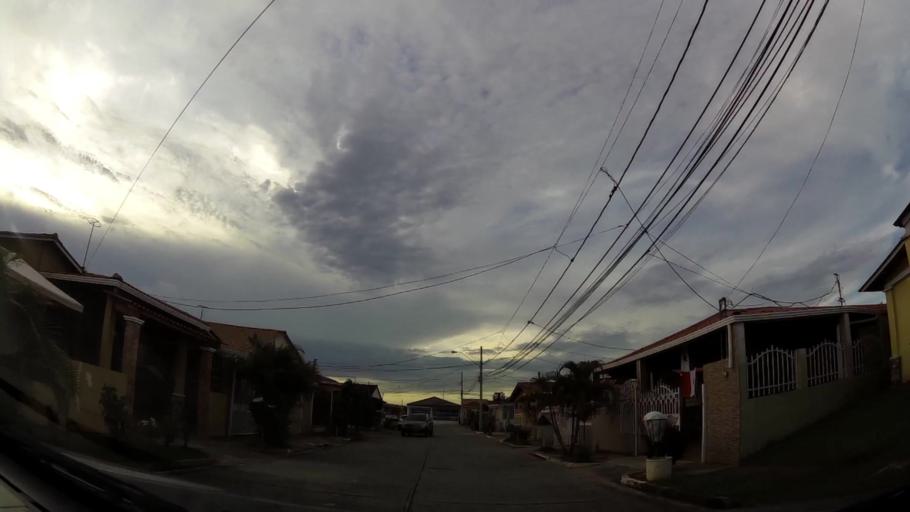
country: PA
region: Panama
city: La Chorrera
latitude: 8.8714
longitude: -79.7661
